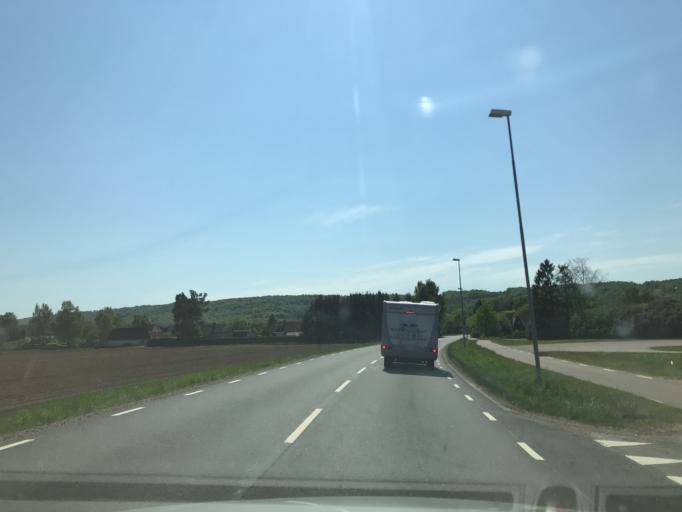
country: SE
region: Skane
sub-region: Klippans Kommun
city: Klippan
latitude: 56.0966
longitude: 13.1477
